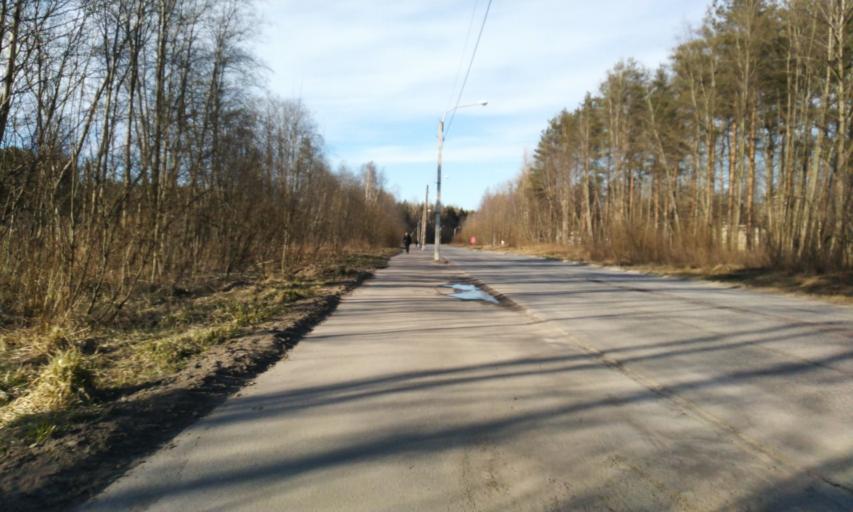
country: RU
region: Leningrad
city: Toksovo
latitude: 60.1143
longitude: 30.4864
